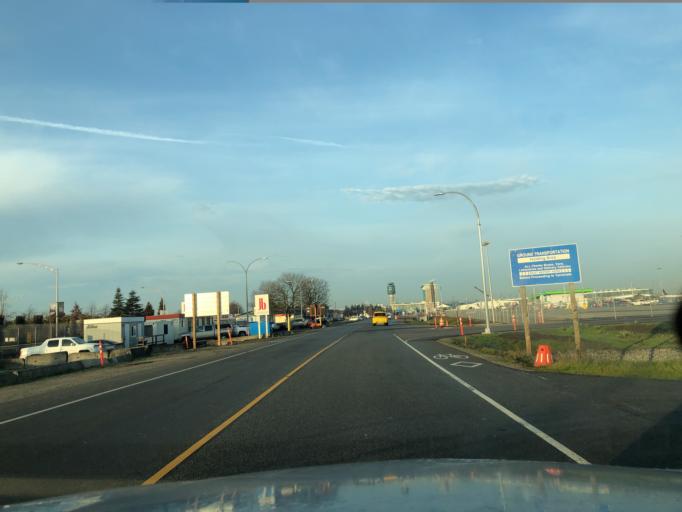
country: CA
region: British Columbia
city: Richmond
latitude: 49.1932
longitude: -123.1623
